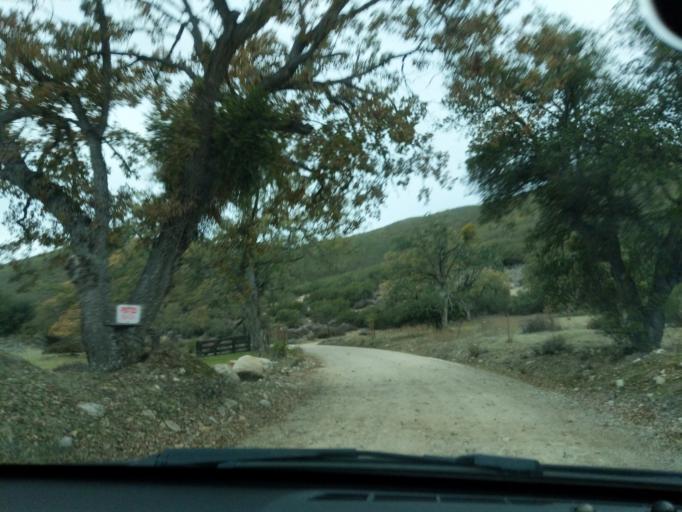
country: US
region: California
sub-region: Monterey County
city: Soledad
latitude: 36.5659
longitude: -121.2068
